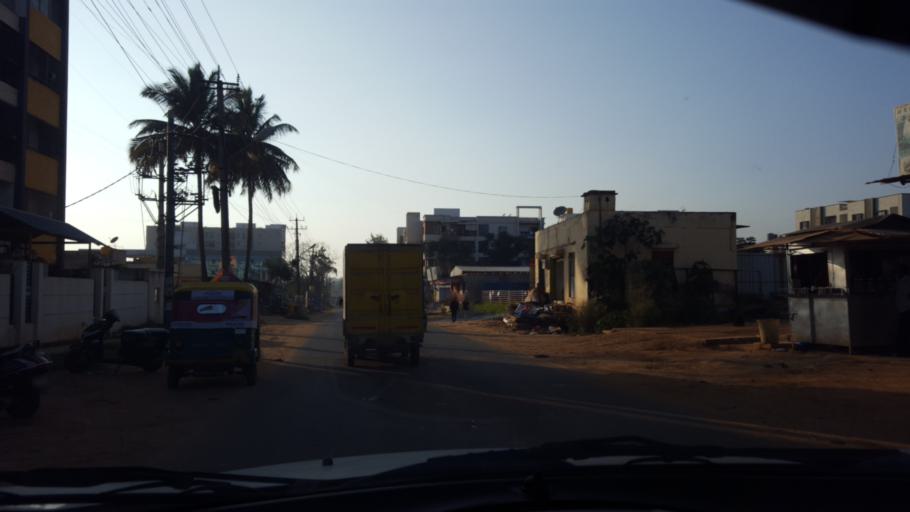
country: IN
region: Karnataka
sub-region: Bangalore Rural
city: Hoskote
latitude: 12.9393
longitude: 77.7387
